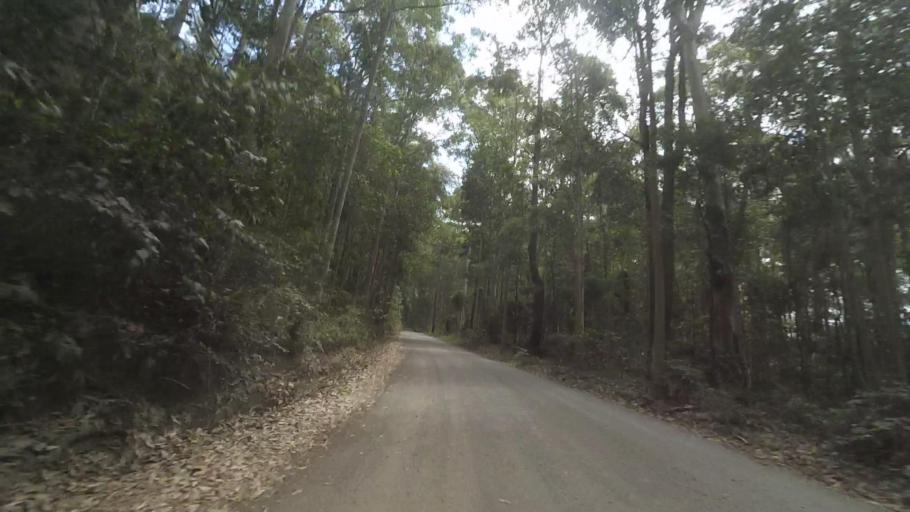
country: AU
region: New South Wales
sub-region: Shoalhaven Shire
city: Milton
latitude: -35.4379
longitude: 150.3248
